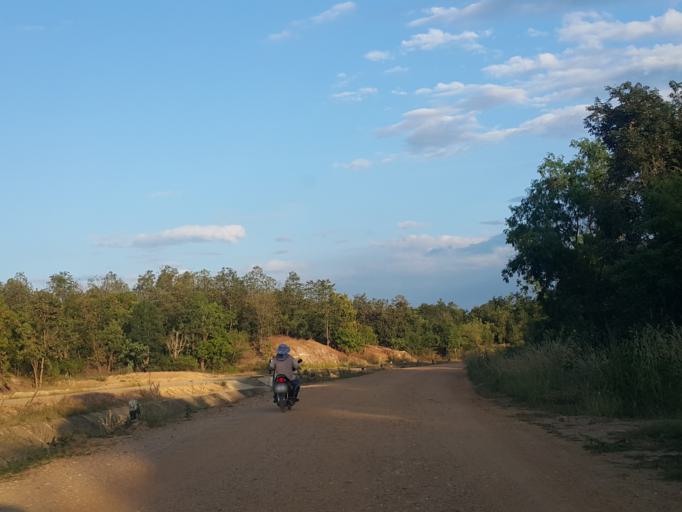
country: TH
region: Lampang
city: Mae Mo
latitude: 18.4340
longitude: 99.5991
